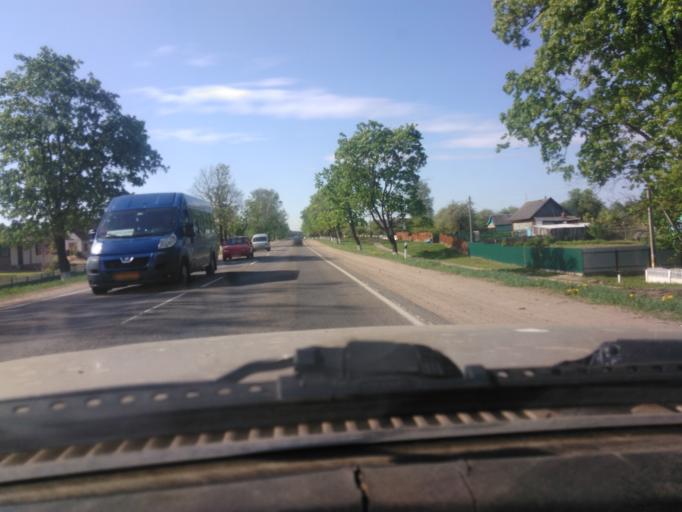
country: BY
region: Mogilev
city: Buynichy
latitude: 53.8280
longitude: 30.2427
